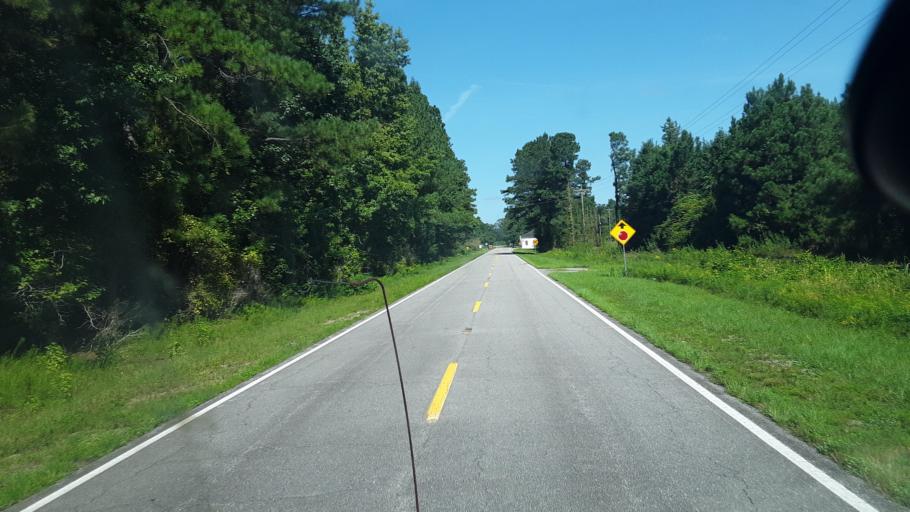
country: US
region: South Carolina
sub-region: Hampton County
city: Varnville
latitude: 32.9461
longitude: -81.0308
